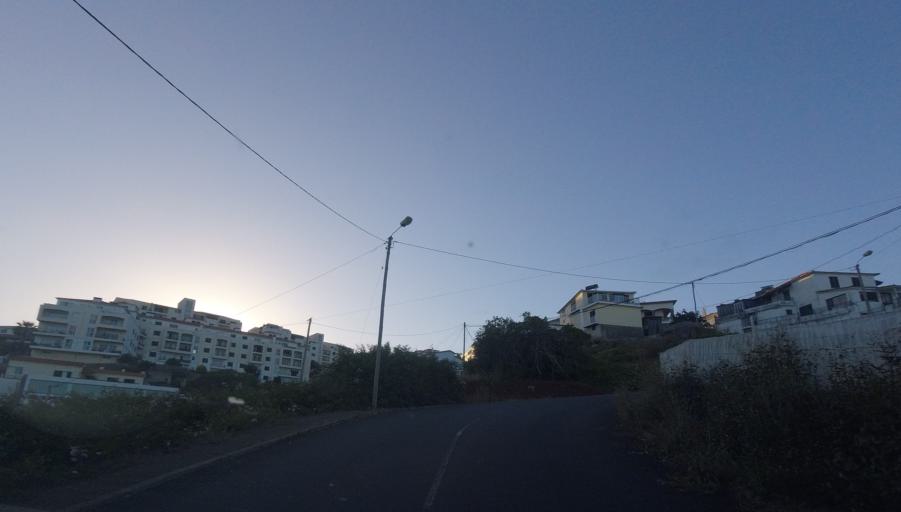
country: PT
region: Madeira
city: Canico
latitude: 32.6465
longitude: -16.8400
